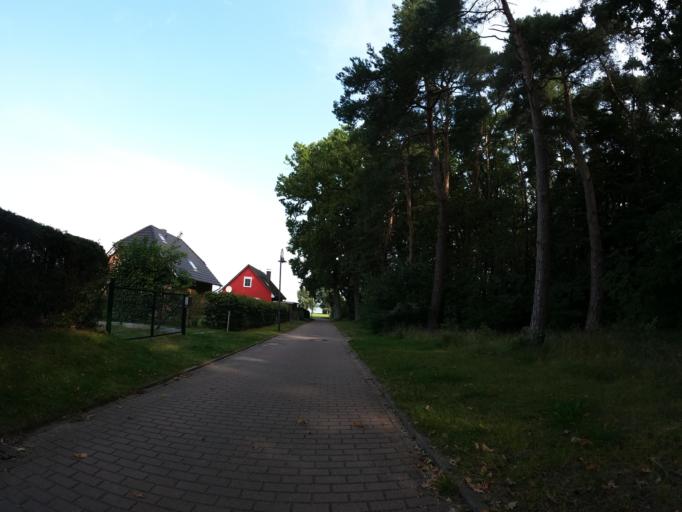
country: DE
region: Mecklenburg-Vorpommern
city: Malchow
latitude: 53.4925
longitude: 12.4962
